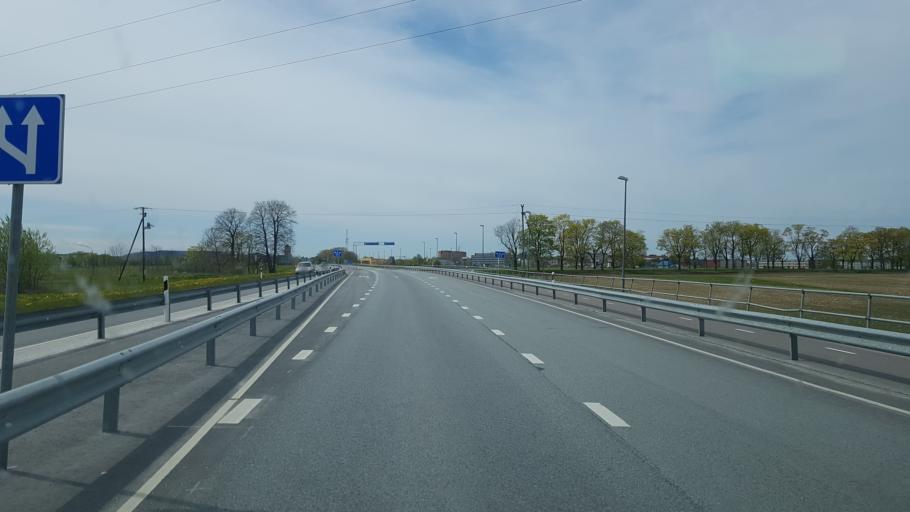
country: EE
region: Ida-Virumaa
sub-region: Kohtla-Jaerve linn
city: Kohtla-Jarve
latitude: 59.4036
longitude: 27.3156
